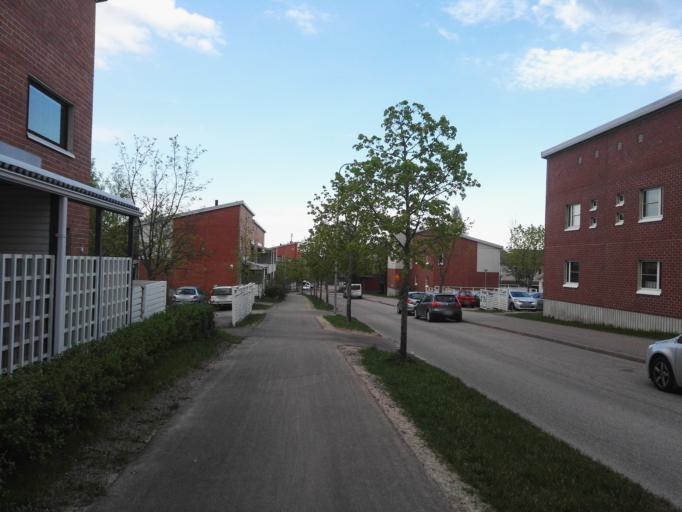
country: FI
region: Paijanne Tavastia
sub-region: Lahti
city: Lahti
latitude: 60.9751
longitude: 25.6470
